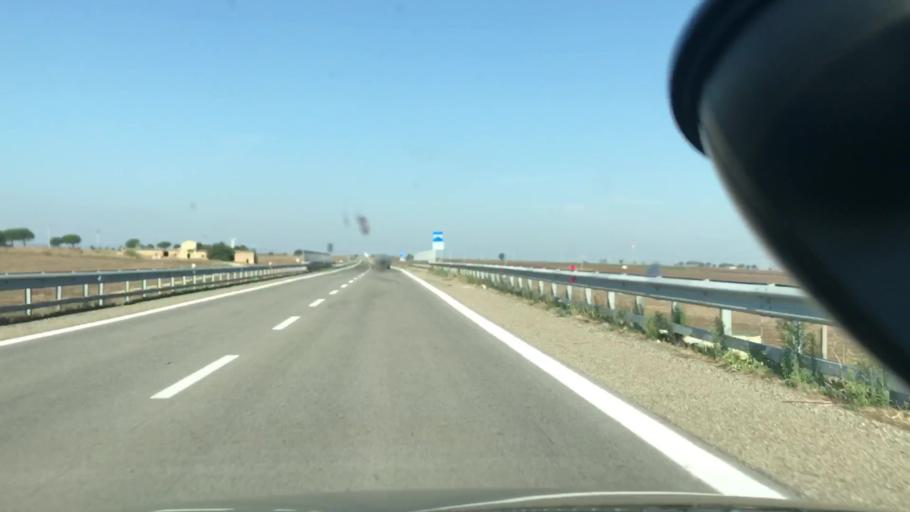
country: IT
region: Basilicate
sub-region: Provincia di Potenza
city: Montemilone
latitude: 40.9870
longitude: 15.9113
